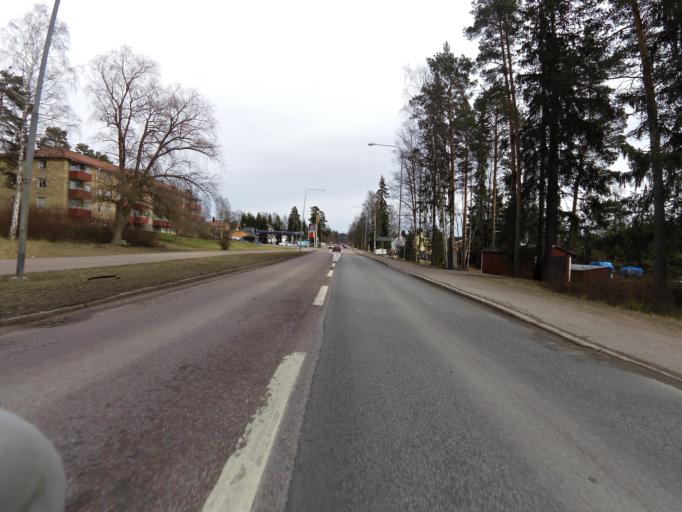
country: SE
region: Gaevleborg
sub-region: Hofors Kommun
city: Hofors
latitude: 60.5416
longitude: 16.2743
